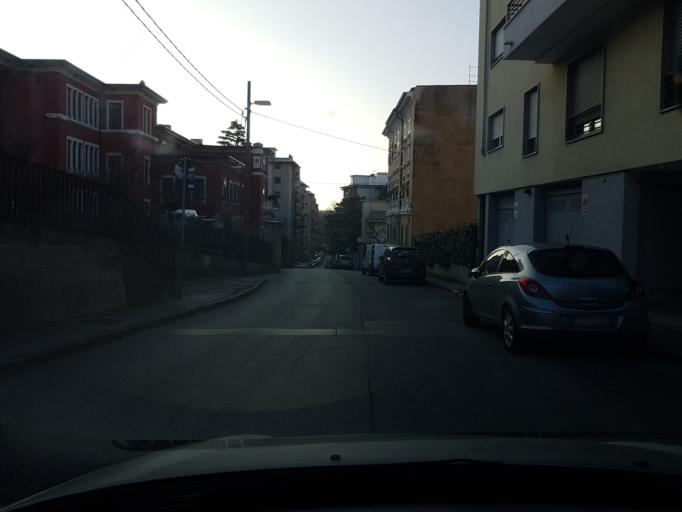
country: IT
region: Friuli Venezia Giulia
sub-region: Provincia di Trieste
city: Trieste
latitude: 45.6544
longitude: 13.8027
